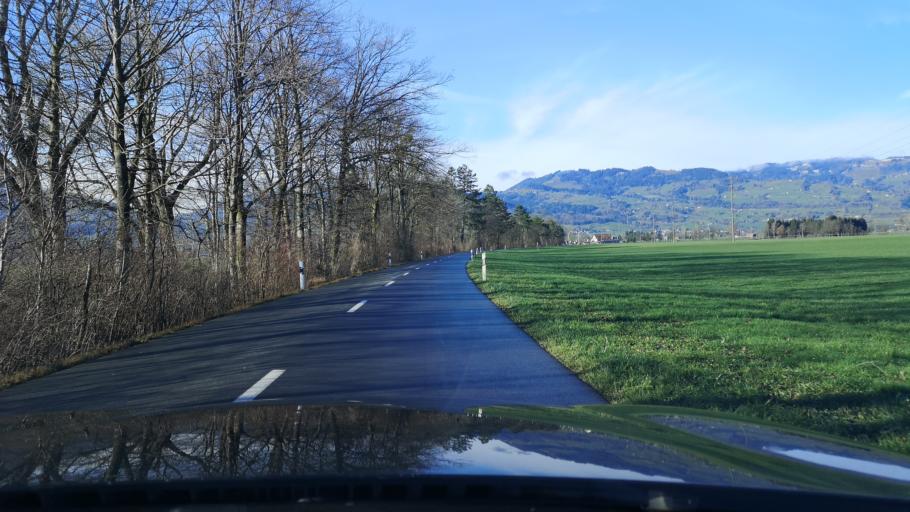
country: CH
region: Saint Gallen
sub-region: Wahlkreis Rheintal
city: Oberriet
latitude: 47.3407
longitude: 9.5739
